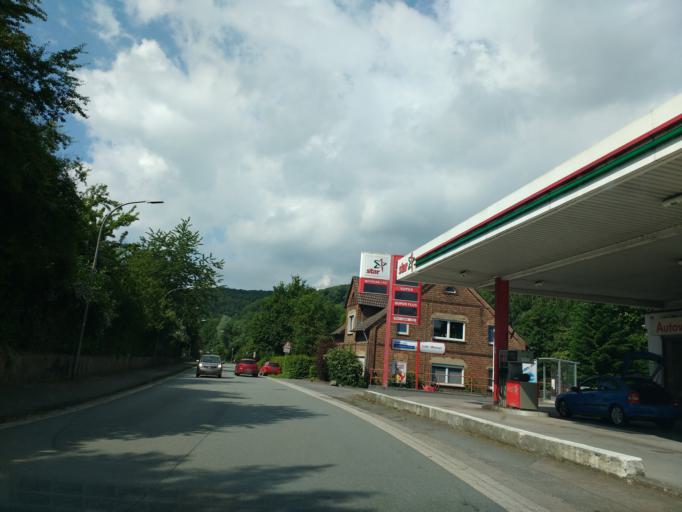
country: DE
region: North Rhine-Westphalia
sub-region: Regierungsbezirk Detmold
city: Dorentrup
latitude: 52.1100
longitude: 8.9529
